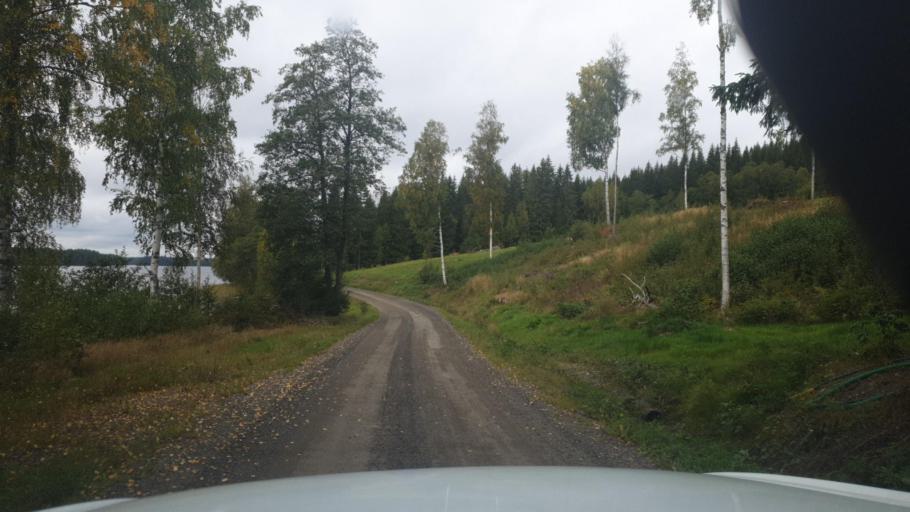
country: SE
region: Vaermland
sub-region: Arvika Kommun
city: Arvika
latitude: 59.8636
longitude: 12.8244
